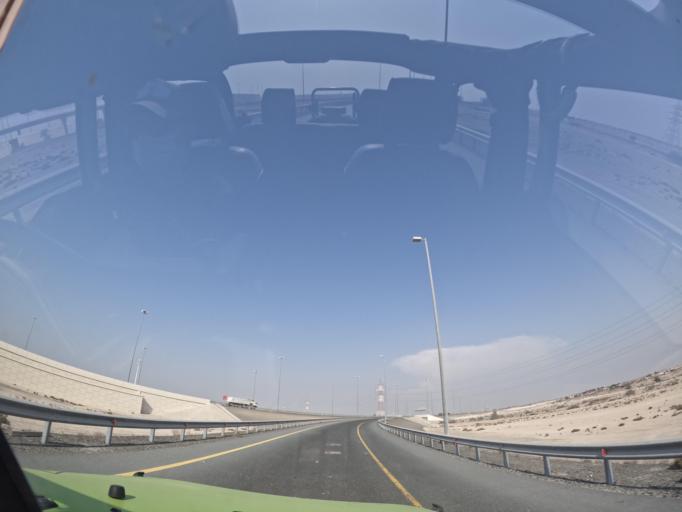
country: AE
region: Abu Dhabi
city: Abu Dhabi
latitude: 24.6776
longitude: 54.8252
